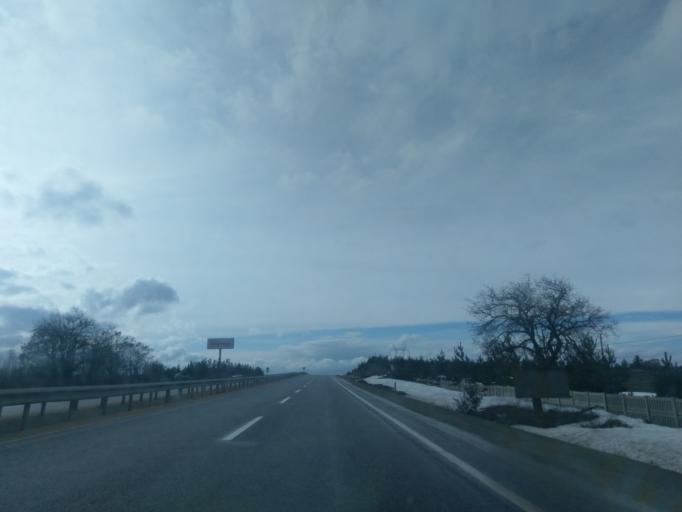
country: TR
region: Eskisehir
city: Inonu
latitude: 39.7199
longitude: 30.2167
